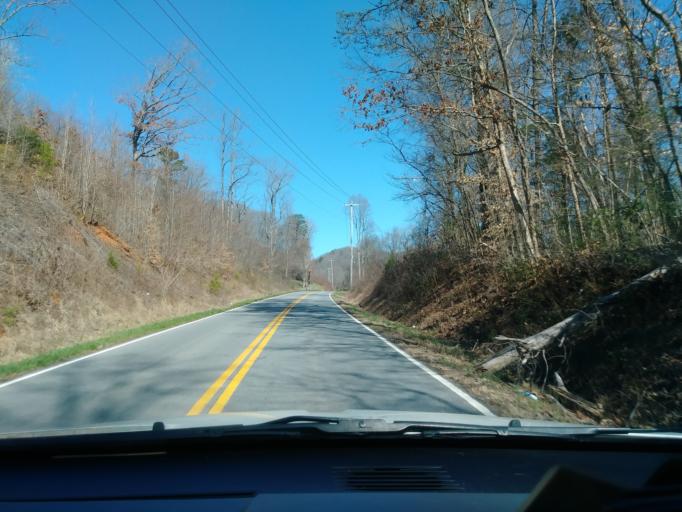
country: US
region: Tennessee
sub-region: Cocke County
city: Newport
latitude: 35.9569
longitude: -83.0492
